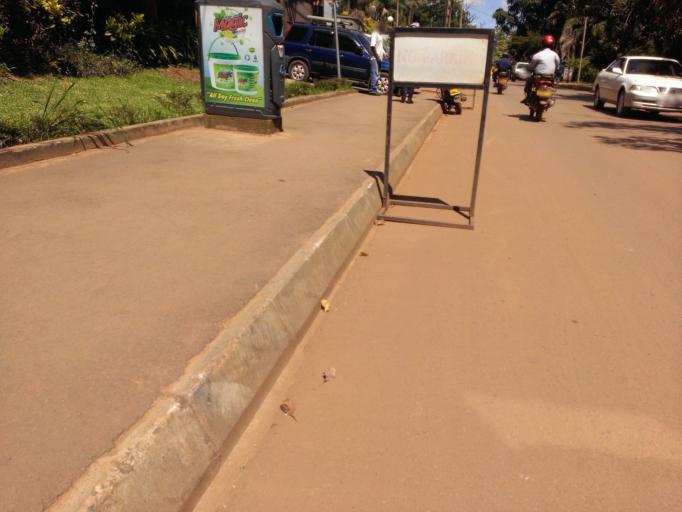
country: UG
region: Central Region
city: Kampala Central Division
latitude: 0.3212
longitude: 32.5778
